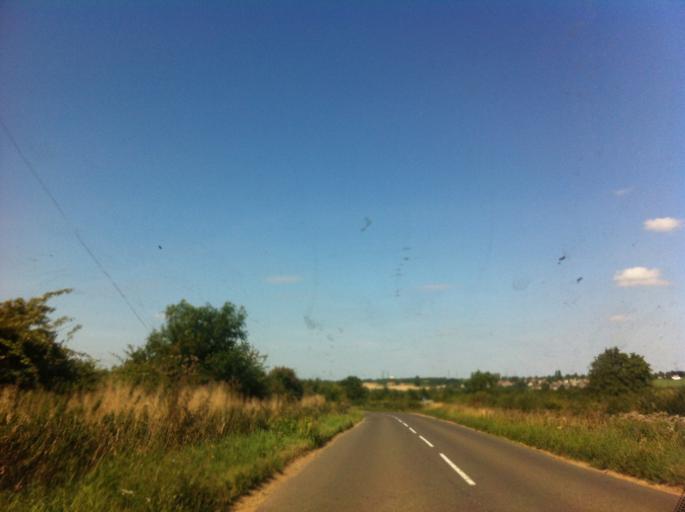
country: GB
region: England
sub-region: Northamptonshire
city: Bozeat
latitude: 52.2604
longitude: -0.6914
